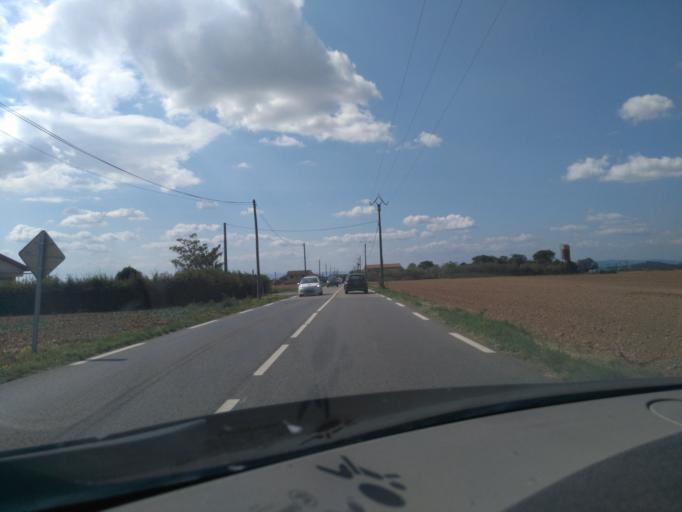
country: FR
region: Rhone-Alpes
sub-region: Departement du Rhone
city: Saint-Laurent-de-Mure
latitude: 45.7194
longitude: 5.0583
